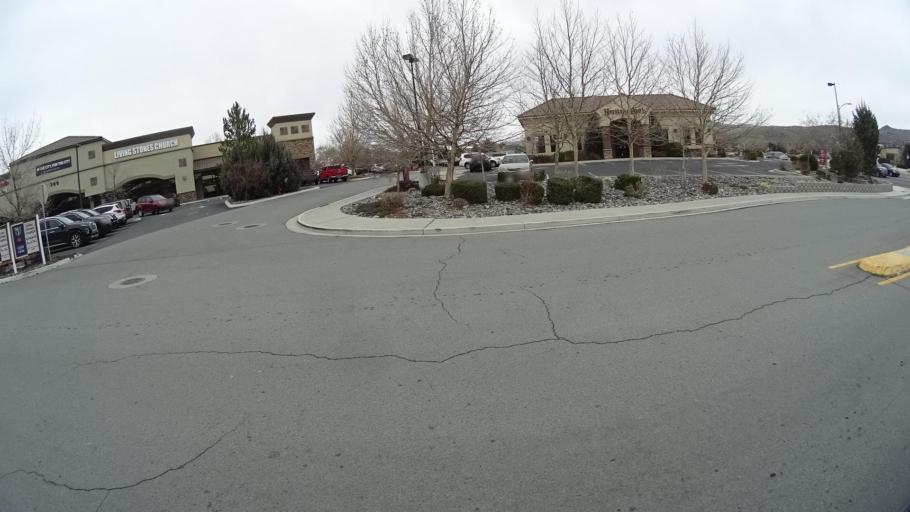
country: US
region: Nevada
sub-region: Washoe County
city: Sun Valley
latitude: 39.5847
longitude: -119.7398
